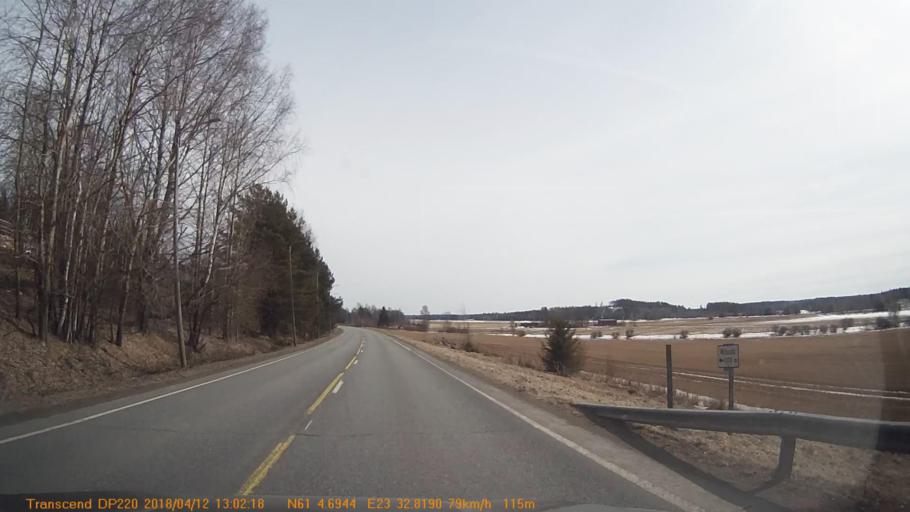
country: FI
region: Pirkanmaa
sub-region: Etelae-Pirkanmaa
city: Urjala
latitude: 61.0781
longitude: 23.5478
